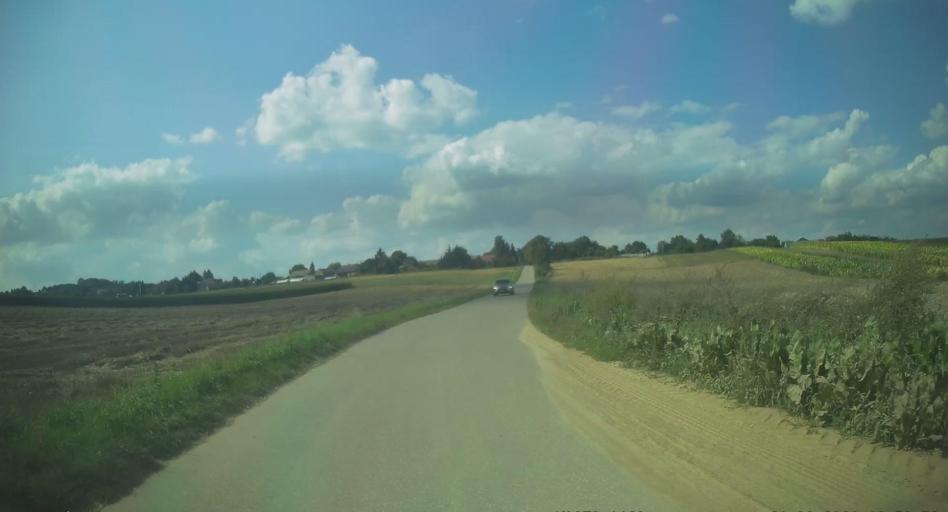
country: PL
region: Lesser Poland Voivodeship
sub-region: Powiat bochenski
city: Dziewin
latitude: 50.1574
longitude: 20.4597
